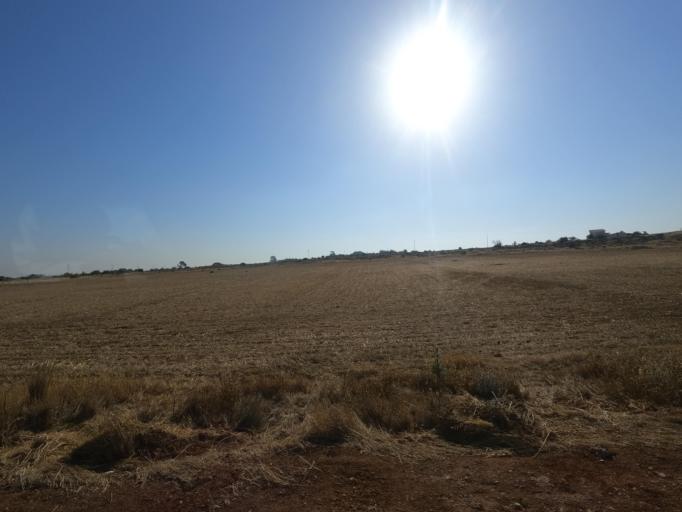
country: CY
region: Ammochostos
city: Frenaros
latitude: 35.0626
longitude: 33.9033
